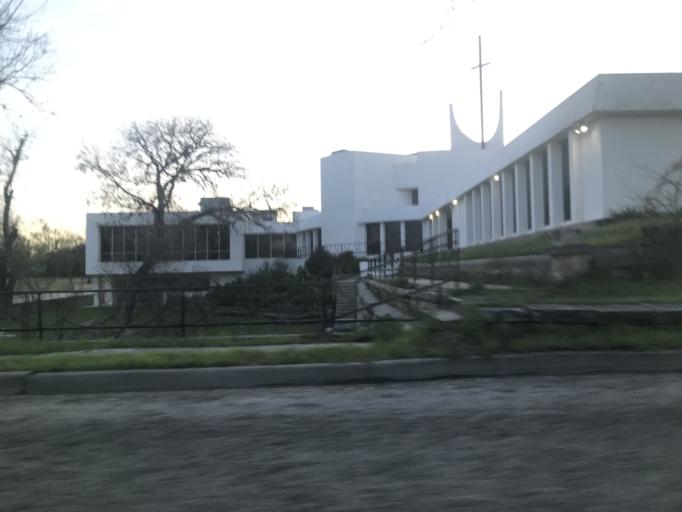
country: US
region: Texas
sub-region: Tom Green County
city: San Angelo
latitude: 31.4590
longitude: -100.4518
